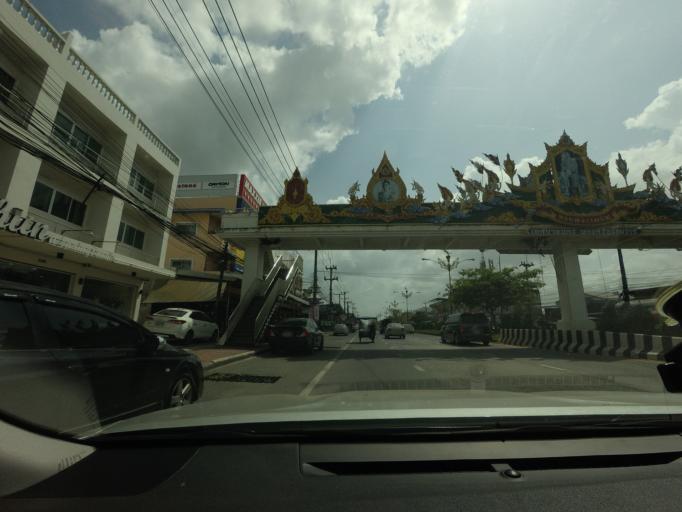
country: TH
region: Nakhon Si Thammarat
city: Nakhon Si Thammarat
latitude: 8.4342
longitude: 99.9323
